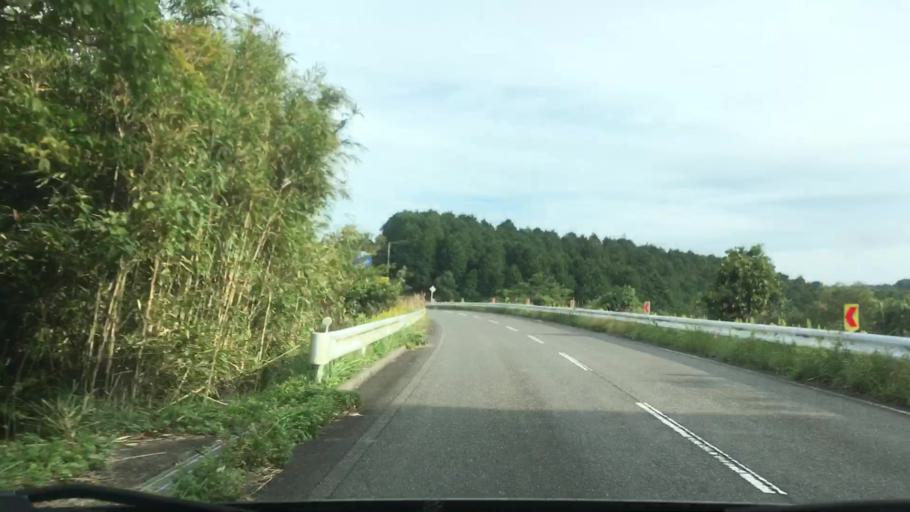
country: JP
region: Nagasaki
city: Sasebo
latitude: 33.0129
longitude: 129.7066
